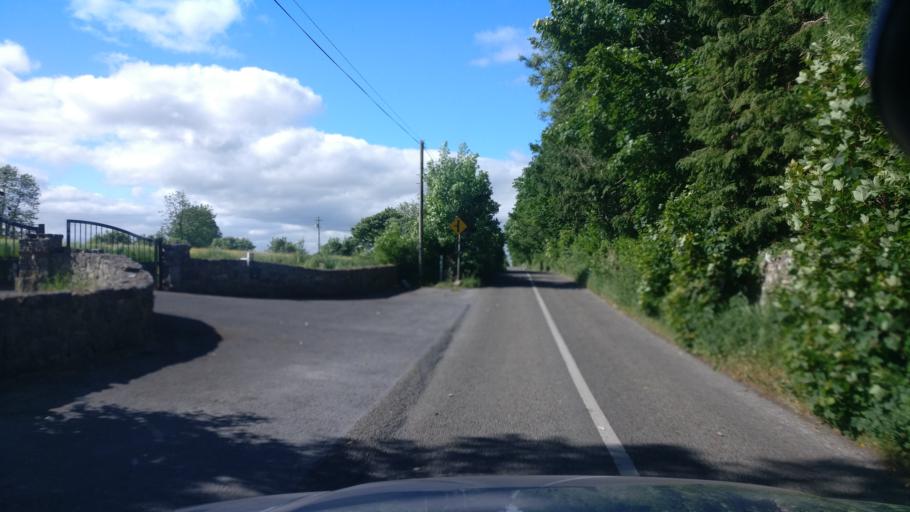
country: IE
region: Connaught
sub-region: County Galway
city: Loughrea
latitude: 53.2350
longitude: -8.6240
